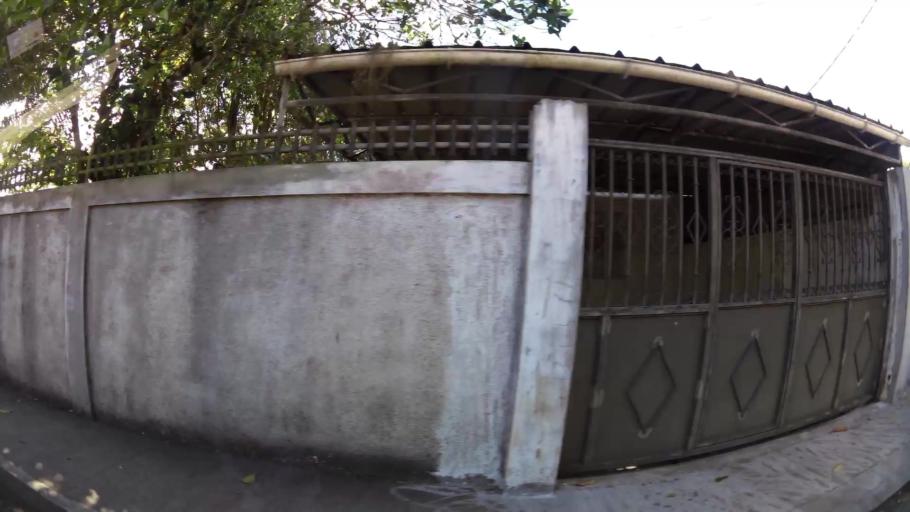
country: MU
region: Plaines Wilhems
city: Vacoas
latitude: -20.3266
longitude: 57.4859
